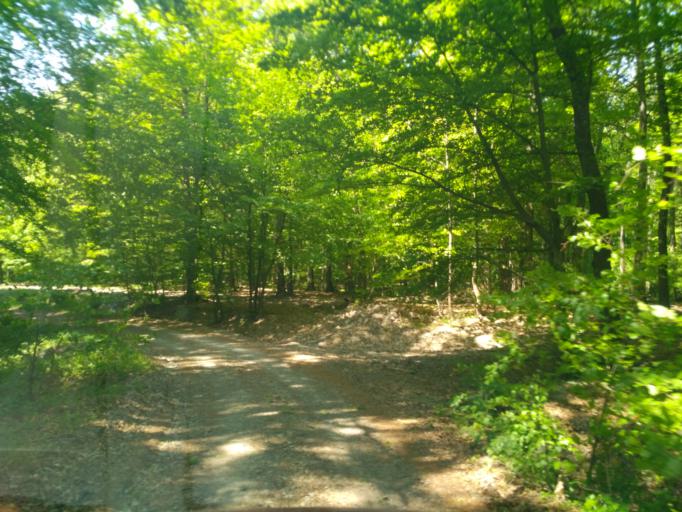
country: SK
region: Presovsky
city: Vranov nad Topl'ou
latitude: 48.8401
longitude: 21.4743
